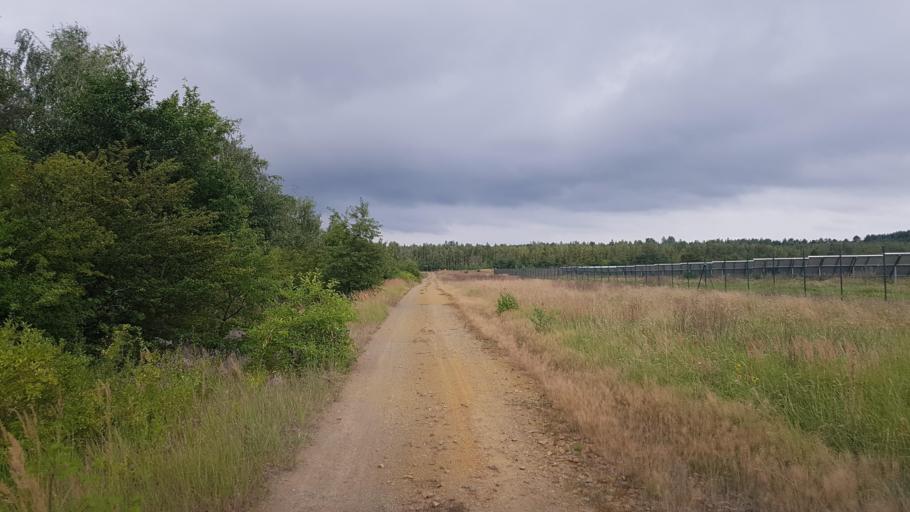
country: DE
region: Brandenburg
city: Finsterwalde
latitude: 51.5647
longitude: 13.7284
